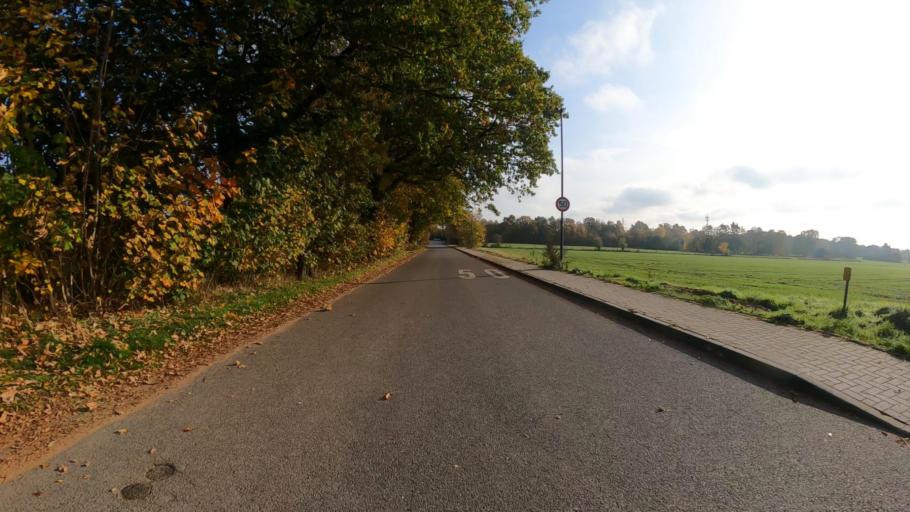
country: DE
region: Lower Saxony
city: Buchholz in der Nordheide
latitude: 53.3327
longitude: 9.8399
